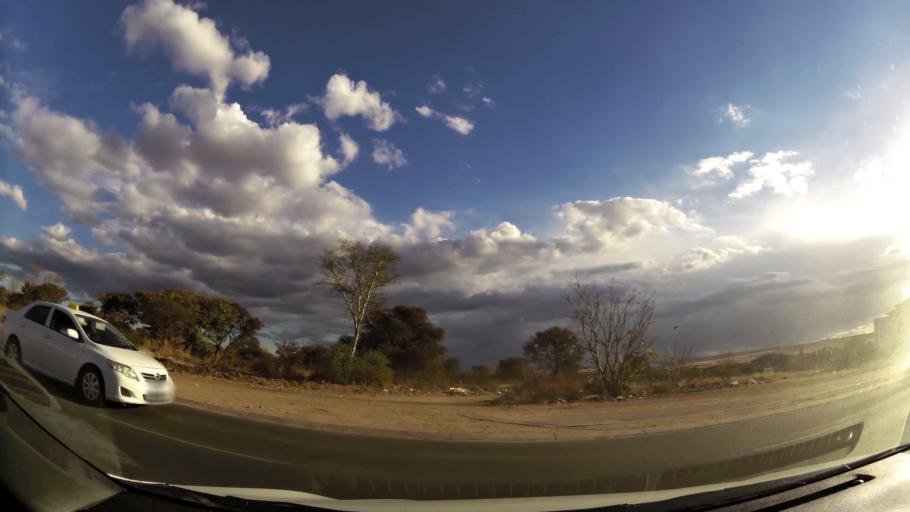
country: ZA
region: Limpopo
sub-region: Capricorn District Municipality
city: Polokwane
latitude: -23.9178
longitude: 29.4290
